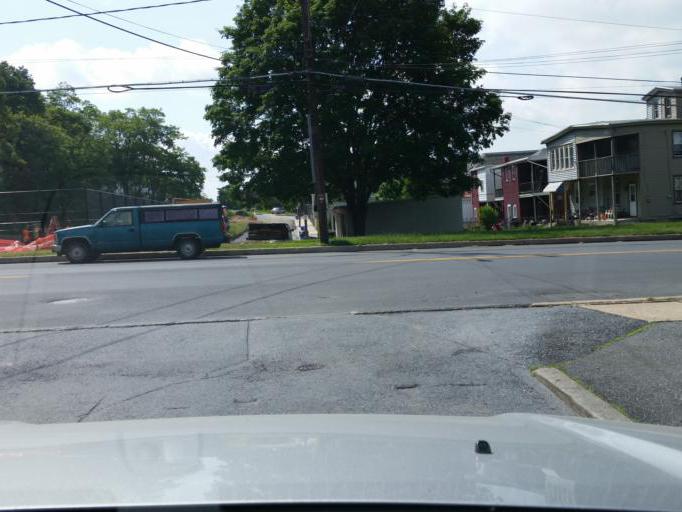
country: US
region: Pennsylvania
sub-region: Dauphin County
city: Enhaut
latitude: 40.2305
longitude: -76.8319
